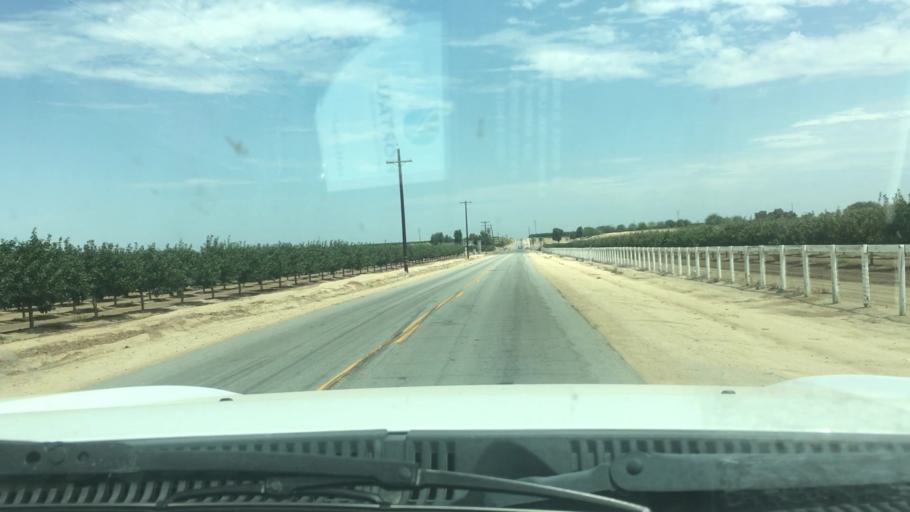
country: US
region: California
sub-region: Kern County
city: Shafter
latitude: 35.5594
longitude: -119.1512
